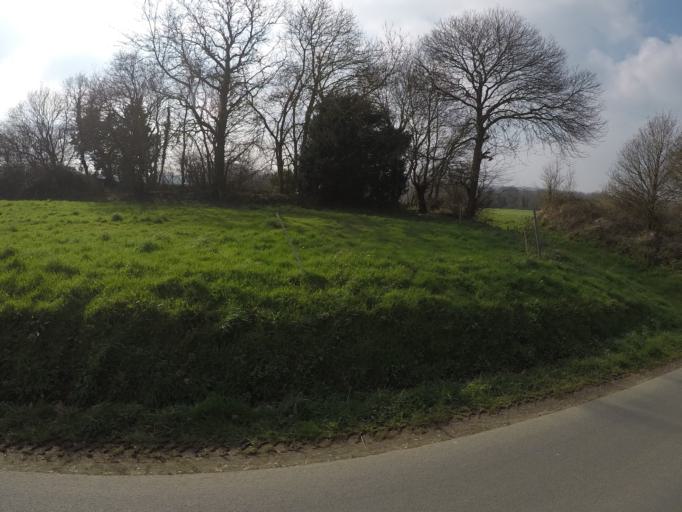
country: FR
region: Brittany
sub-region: Departement des Cotes-d'Armor
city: Goudelin
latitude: 48.6069
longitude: -3.0280
